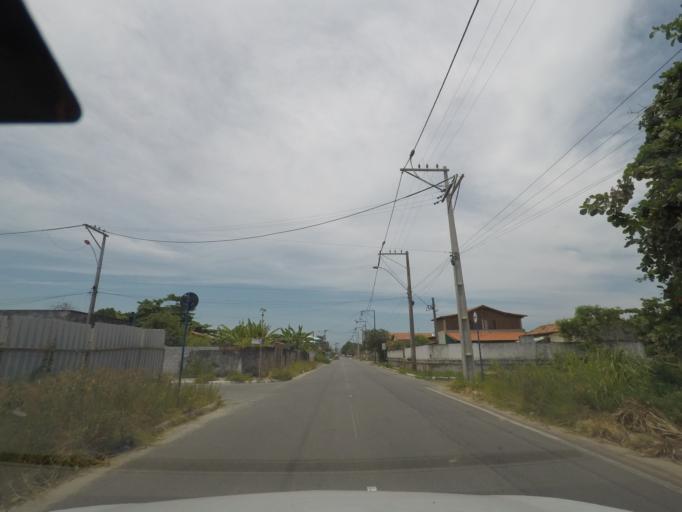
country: BR
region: Rio de Janeiro
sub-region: Marica
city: Marica
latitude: -22.9681
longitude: -42.9605
